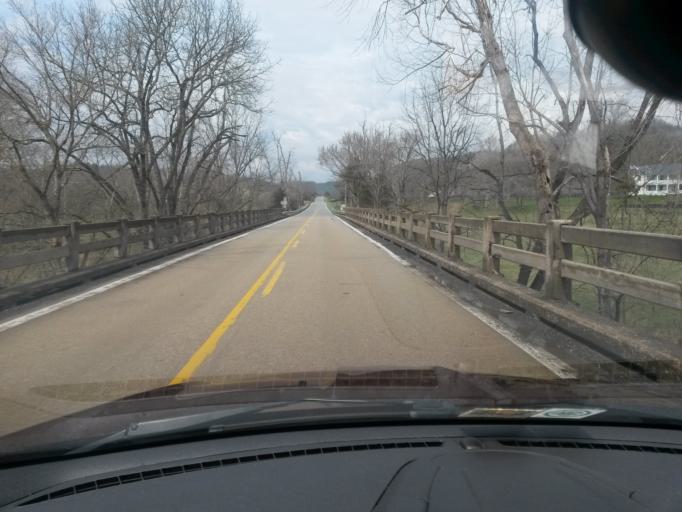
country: US
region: Virginia
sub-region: Bath County
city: Warm Springs
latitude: 38.0145
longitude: -79.6405
